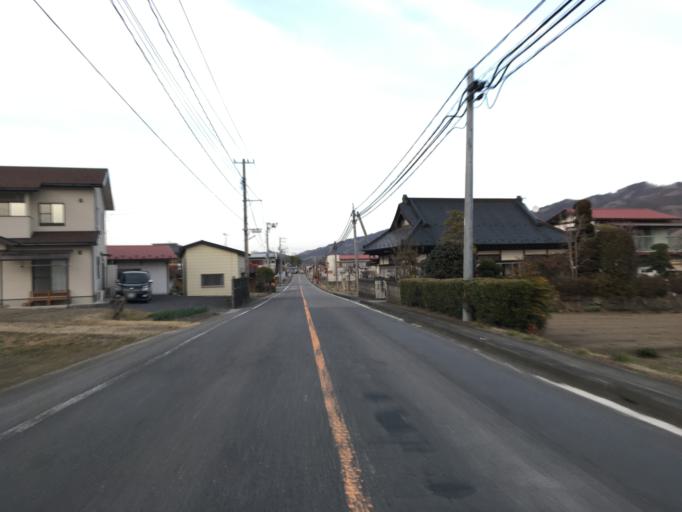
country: JP
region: Ibaraki
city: Daigo
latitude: 36.9077
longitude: 140.4074
